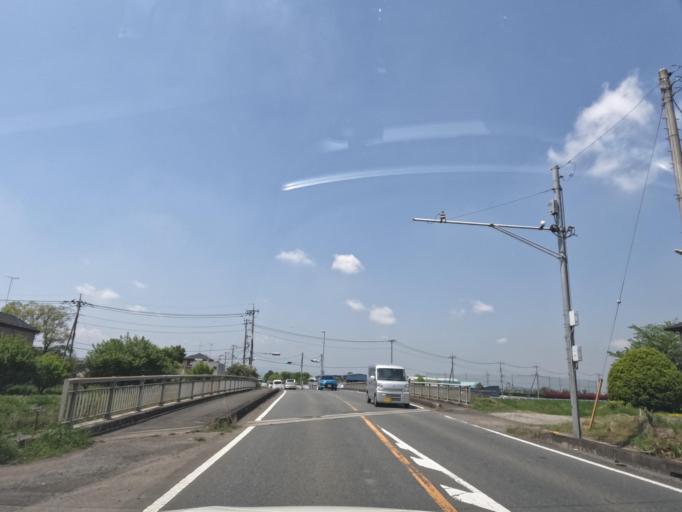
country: JP
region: Saitama
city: Kawagoe
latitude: 35.9647
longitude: 139.4906
